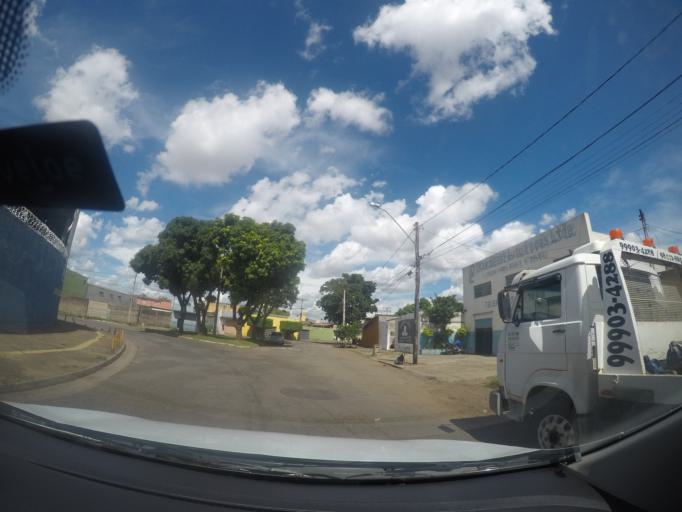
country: BR
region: Goias
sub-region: Goiania
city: Goiania
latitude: -16.6693
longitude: -49.3076
